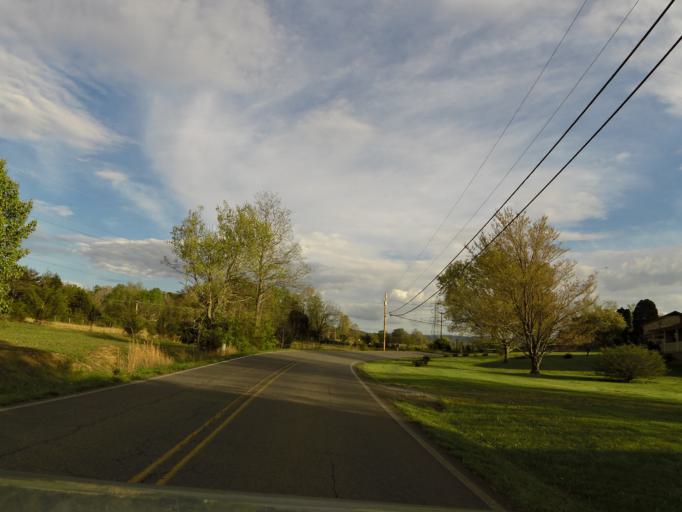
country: US
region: Tennessee
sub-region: Blount County
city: Maryville
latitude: 35.6815
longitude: -84.0128
